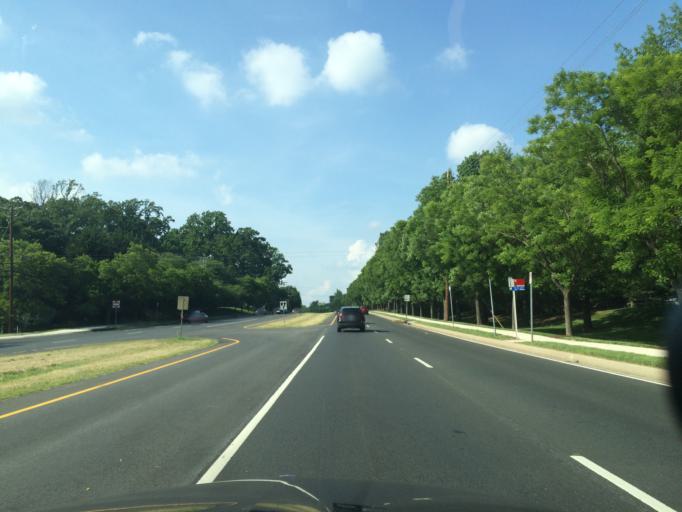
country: US
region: Maryland
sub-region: Montgomery County
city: Olney
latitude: 39.1387
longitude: -77.0684
